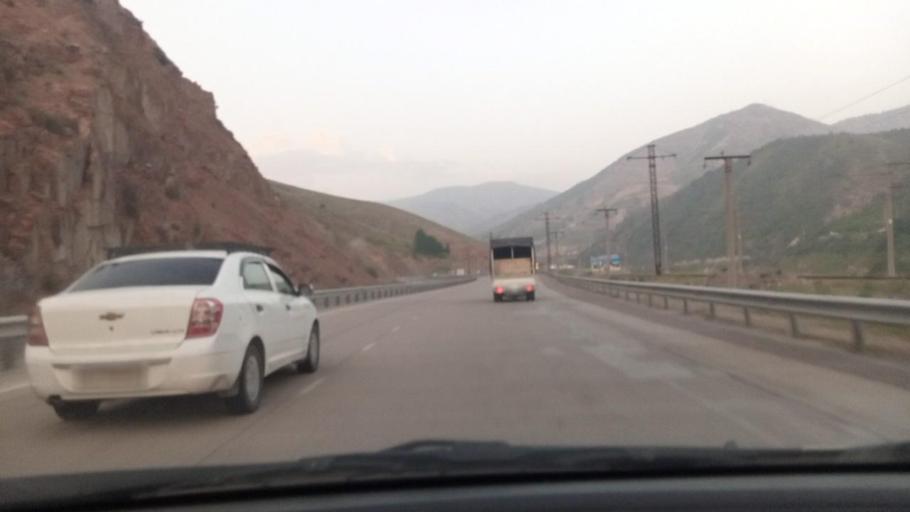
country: UZ
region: Toshkent
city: Angren
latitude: 41.1497
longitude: 70.4208
